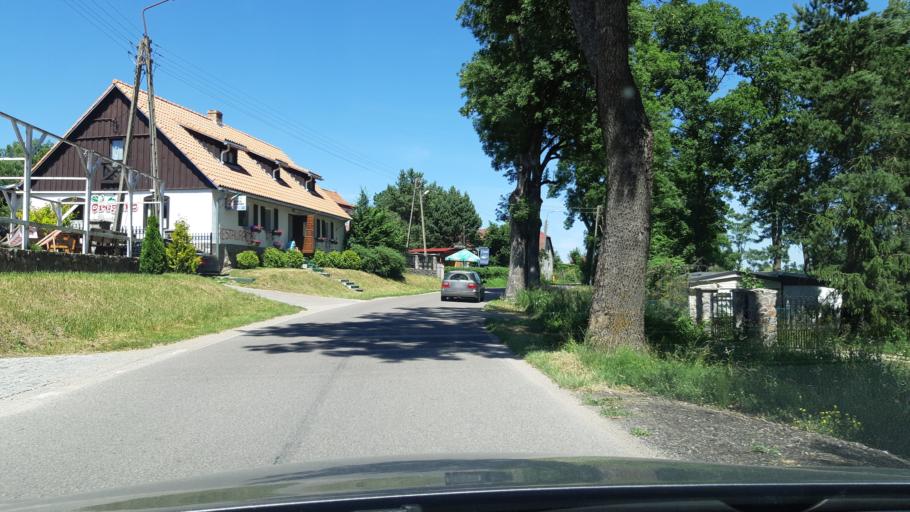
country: PL
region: Warmian-Masurian Voivodeship
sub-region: Powiat gizycki
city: Gizycko
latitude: 53.9489
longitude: 21.7224
